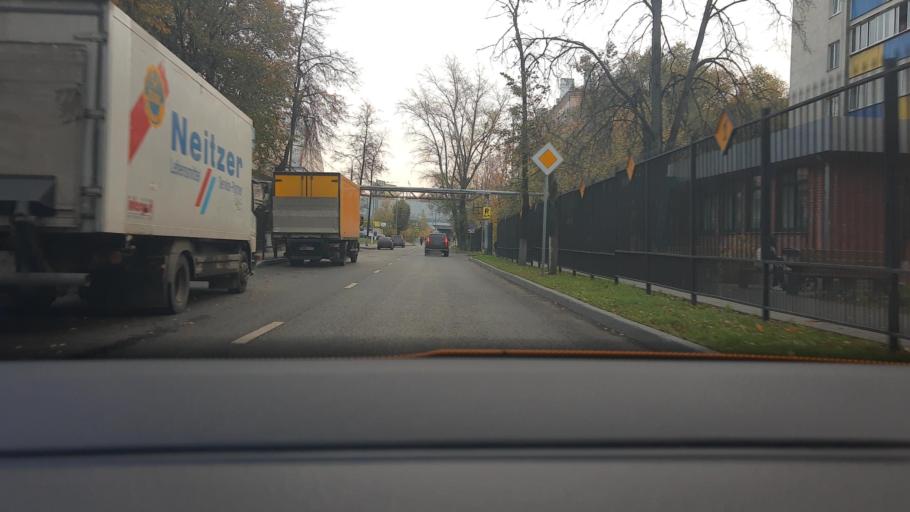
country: RU
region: Moscow
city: Khimki
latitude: 55.8848
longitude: 37.4530
